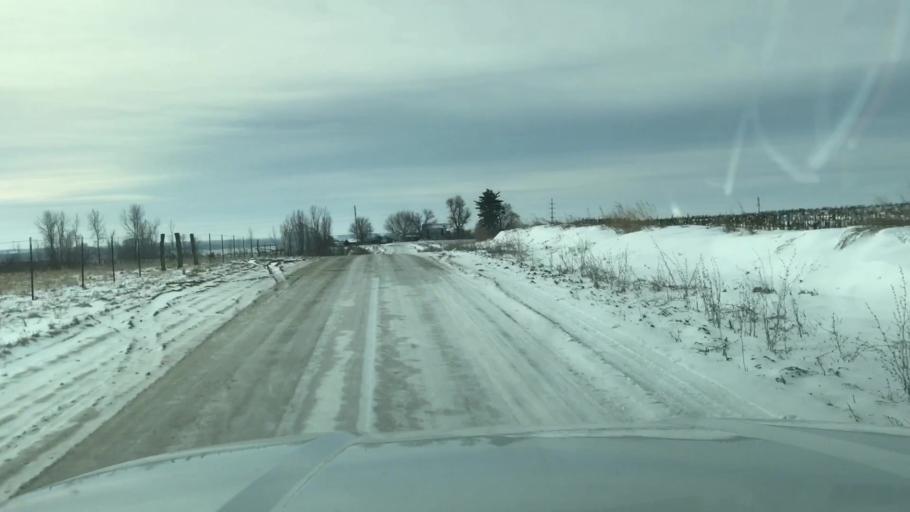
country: US
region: Missouri
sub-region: Holt County
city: Mound City
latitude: 40.1330
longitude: -95.0696
